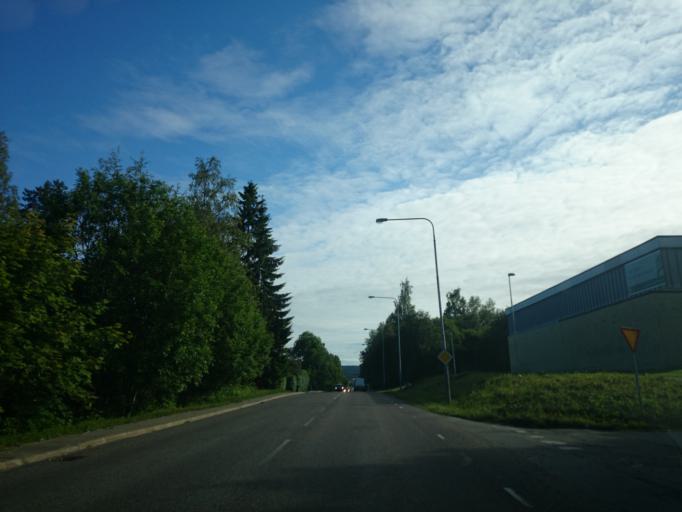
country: SE
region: Vaesternorrland
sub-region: Sundsvalls Kommun
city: Sundsvall
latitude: 62.4072
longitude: 17.3327
